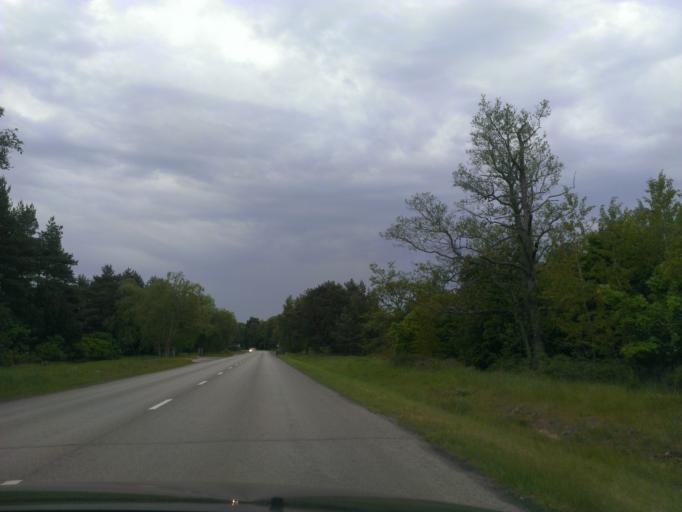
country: LT
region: Klaipedos apskritis
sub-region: Klaipeda
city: Palanga
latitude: 55.8835
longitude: 21.0626
